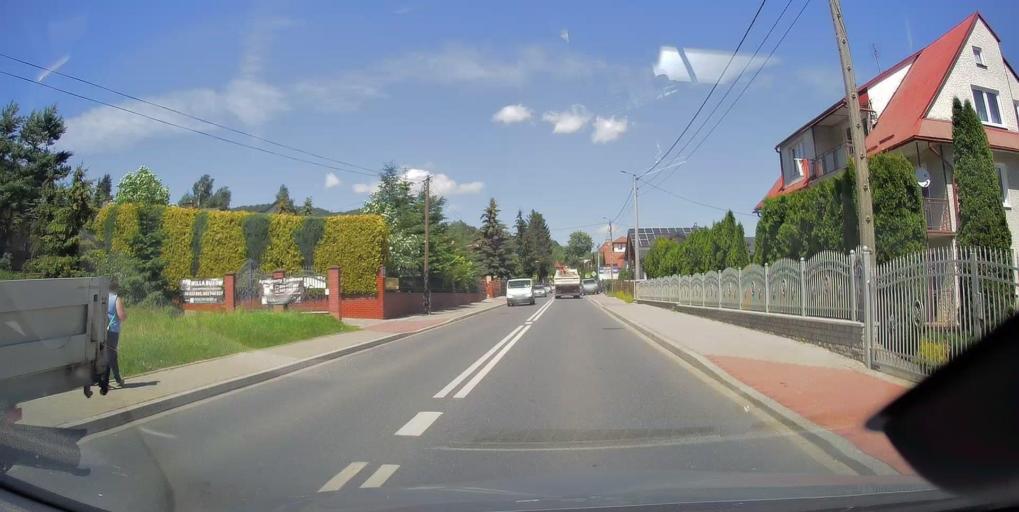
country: PL
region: Lesser Poland Voivodeship
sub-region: Powiat nowosadecki
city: Krynica-Zdroj
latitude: 49.4026
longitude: 20.9532
